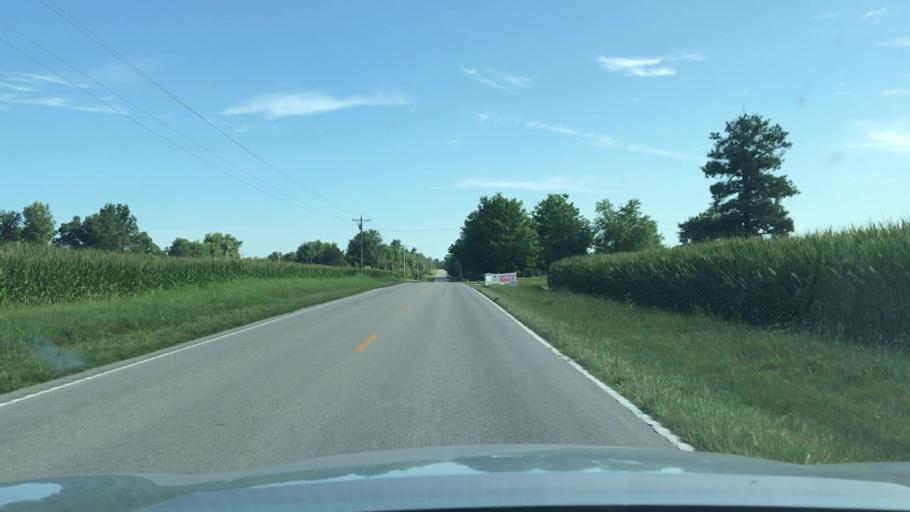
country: US
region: Kentucky
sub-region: Todd County
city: Elkton
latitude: 36.9219
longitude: -87.1627
